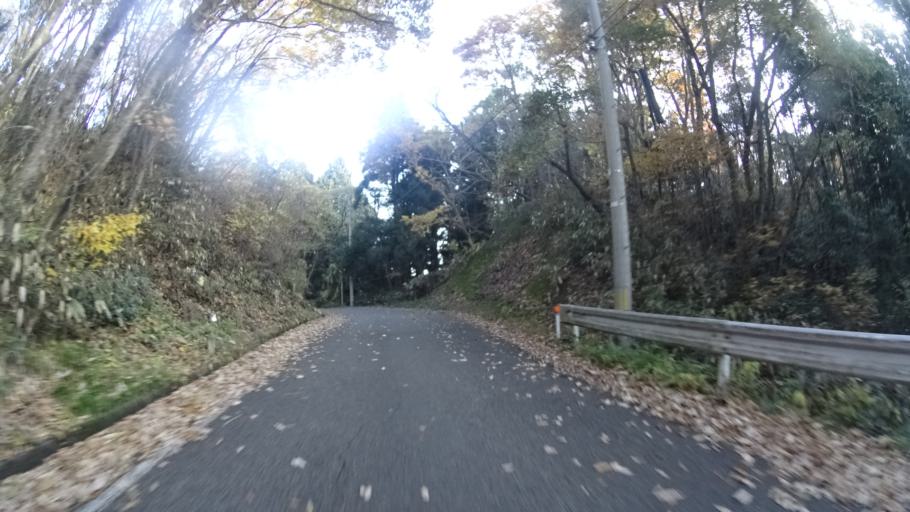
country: JP
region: Niigata
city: Yoshida-kasugacho
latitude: 37.6578
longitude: 138.8134
